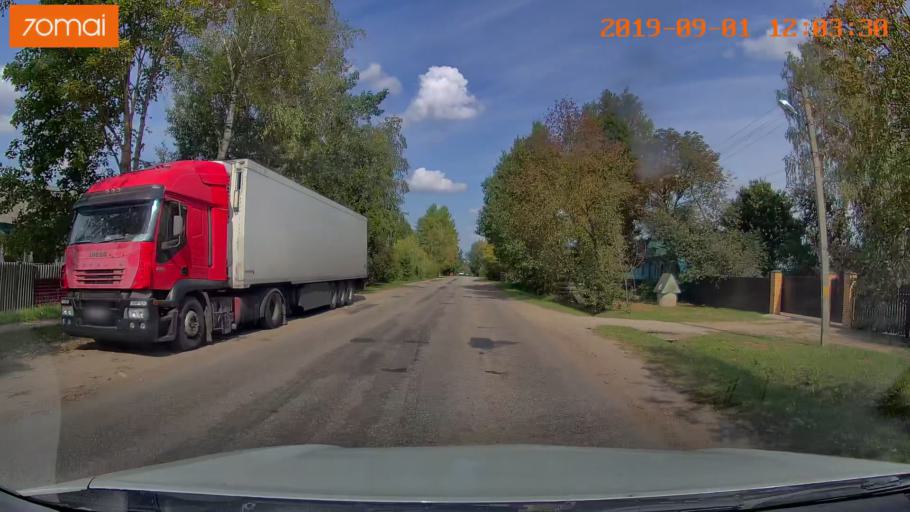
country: RU
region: Kaluga
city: Maloyaroslavets
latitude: 54.9897
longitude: 36.4709
